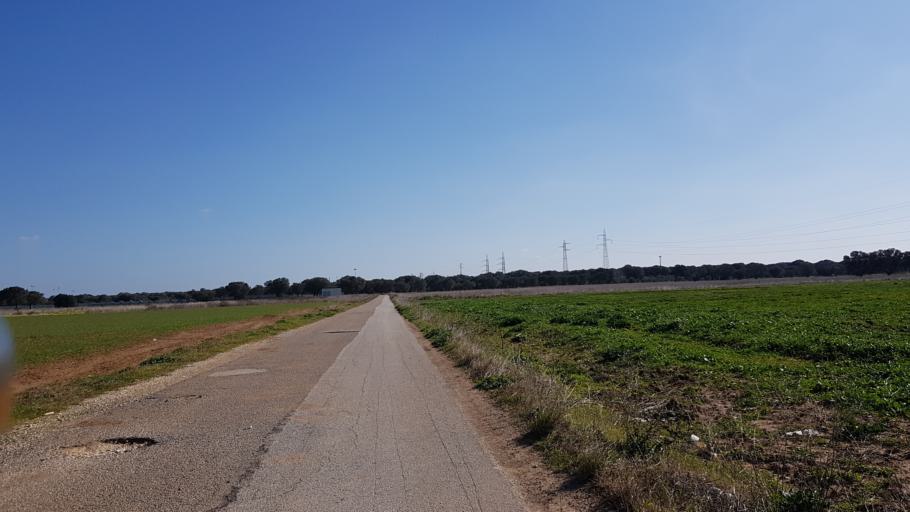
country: IT
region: Apulia
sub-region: Provincia di Brindisi
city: Mesagne
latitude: 40.6203
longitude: 17.8304
